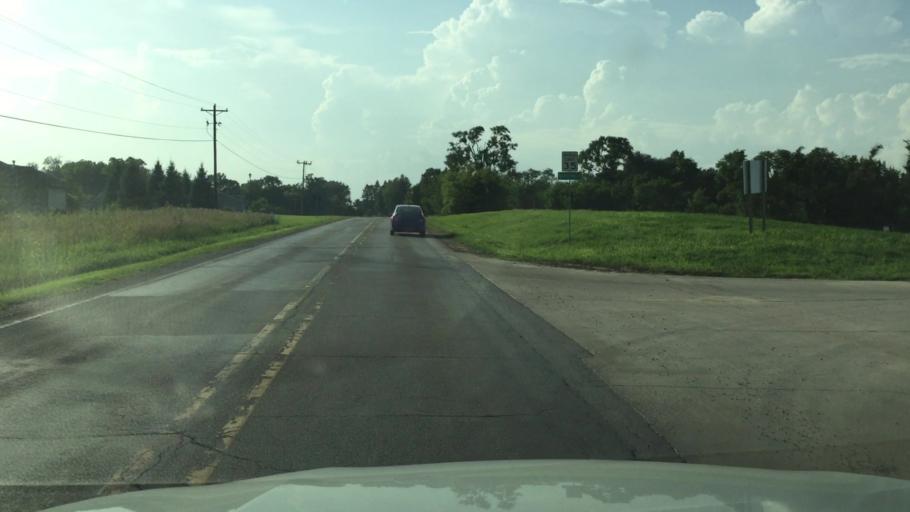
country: US
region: Iowa
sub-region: Linn County
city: Ely
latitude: 41.8375
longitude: -91.6378
